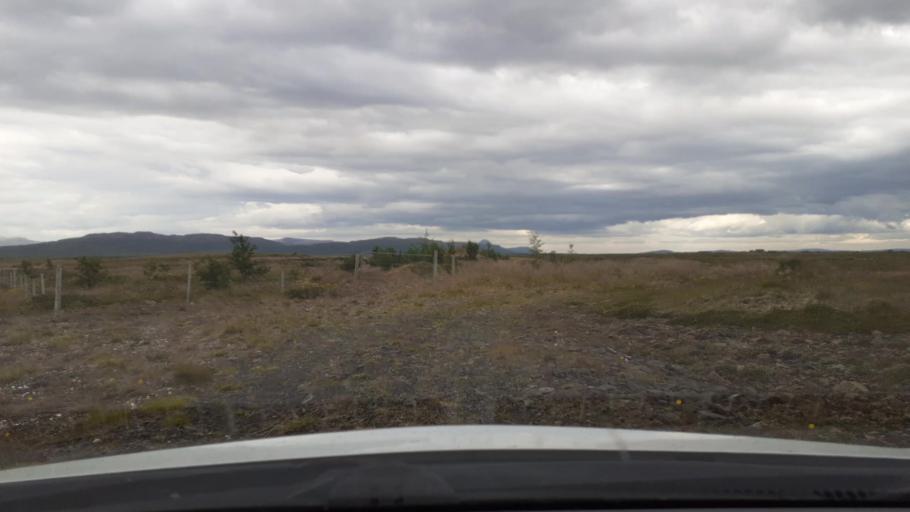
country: IS
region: West
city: Borgarnes
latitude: 64.6588
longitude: -21.8720
